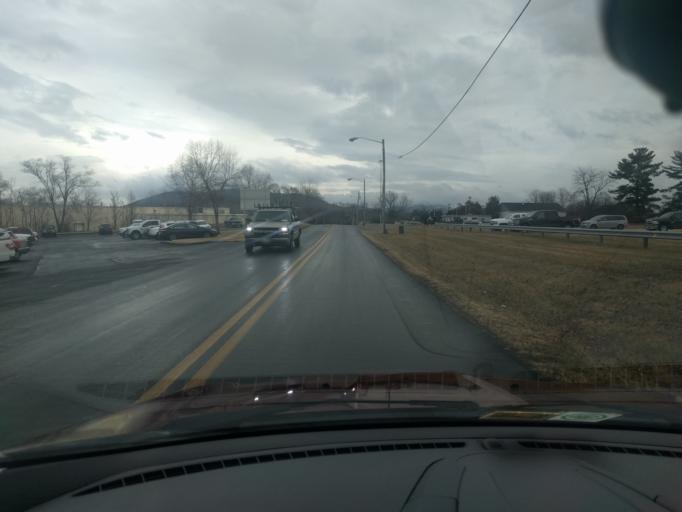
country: US
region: Virginia
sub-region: Roanoke County
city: Hollins
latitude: 37.3242
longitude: -79.9678
